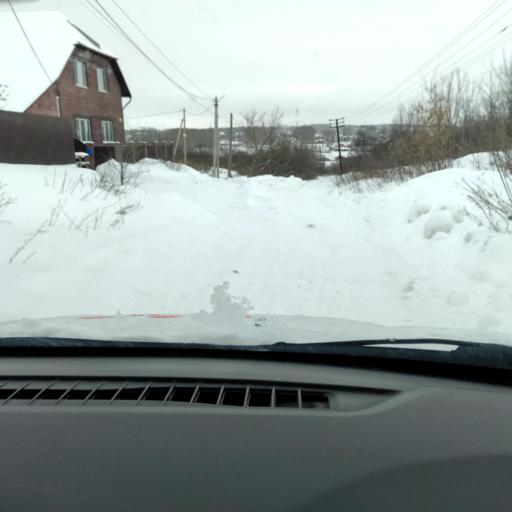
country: RU
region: Bashkortostan
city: Blagoveshchensk
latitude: 55.0501
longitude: 55.9755
